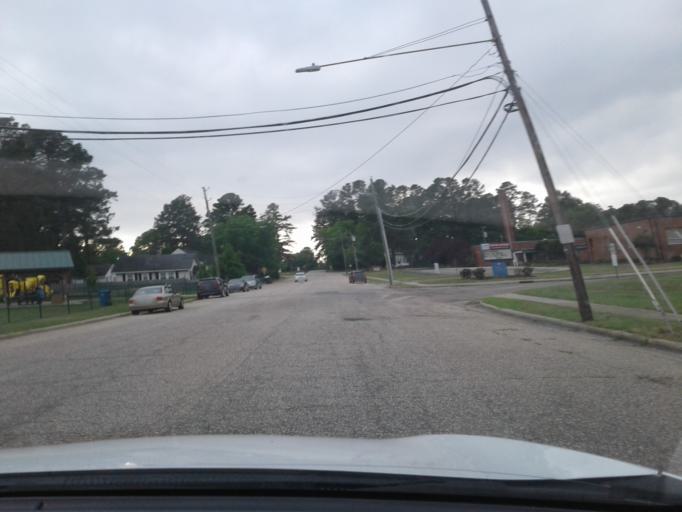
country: US
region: North Carolina
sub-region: Harnett County
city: Dunn
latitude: 35.3148
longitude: -78.6171
